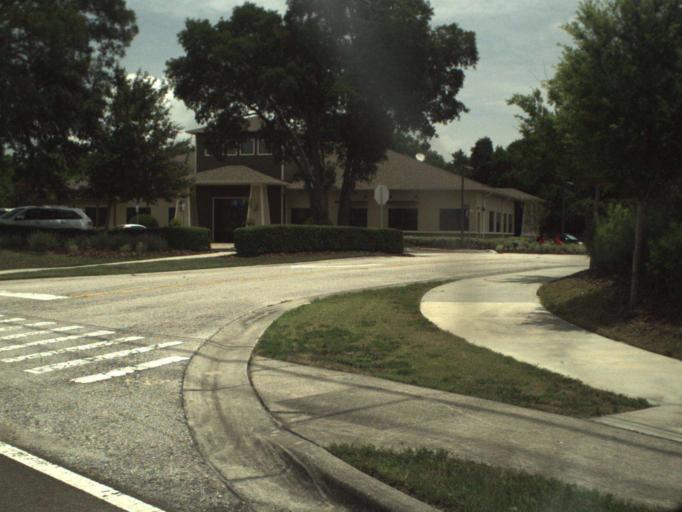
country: US
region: Florida
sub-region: Seminole County
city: Goldenrod
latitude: 28.6244
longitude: -81.2459
